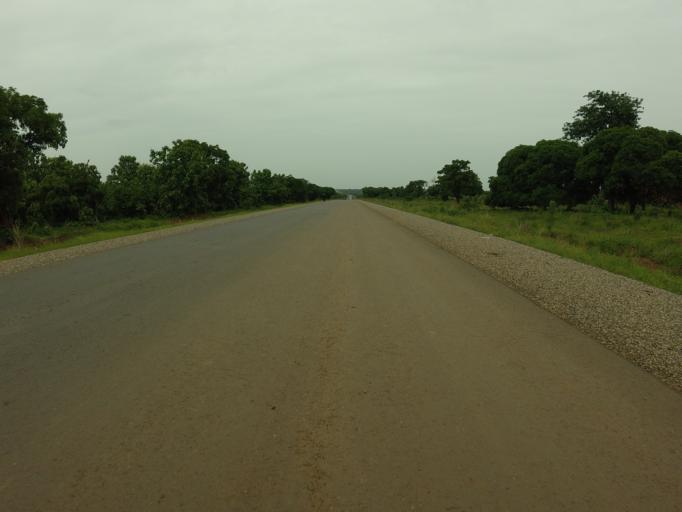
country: GH
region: Northern
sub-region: Yendi
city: Yendi
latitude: 9.2746
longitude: 0.0181
